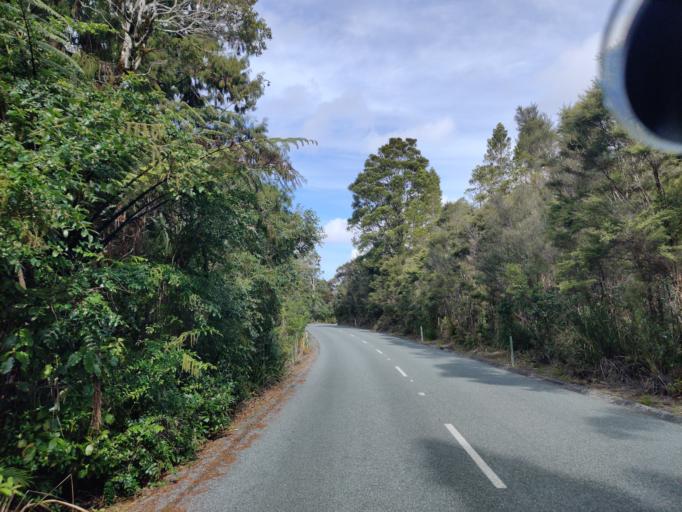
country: NZ
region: Northland
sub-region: Far North District
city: Waimate North
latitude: -35.6095
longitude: 173.5412
